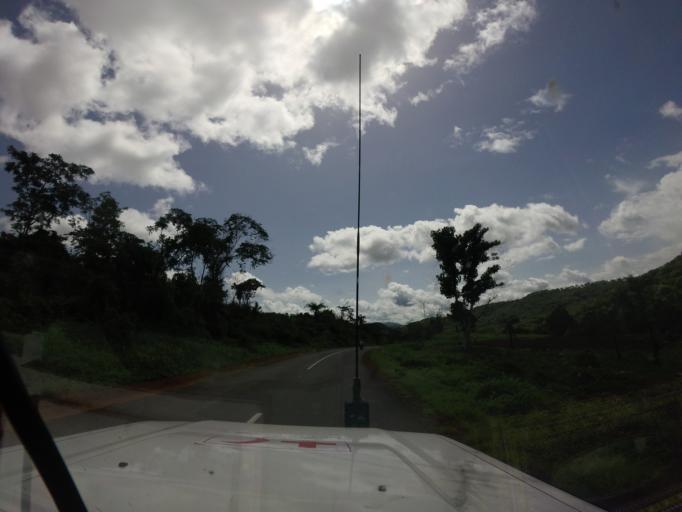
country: GN
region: Mamou
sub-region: Mamou Prefecture
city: Mamou
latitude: 10.1756
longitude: -11.8057
